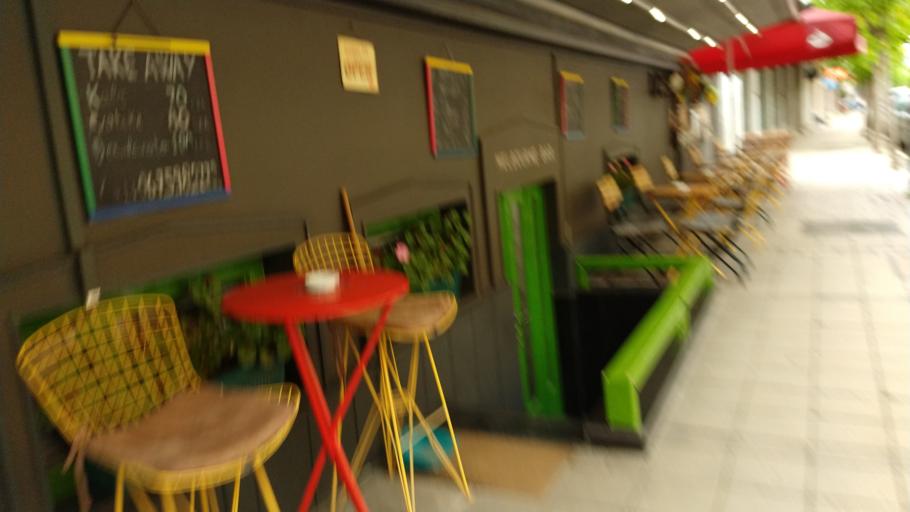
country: AL
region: Tirane
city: Tirana
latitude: 41.3307
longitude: 19.8133
